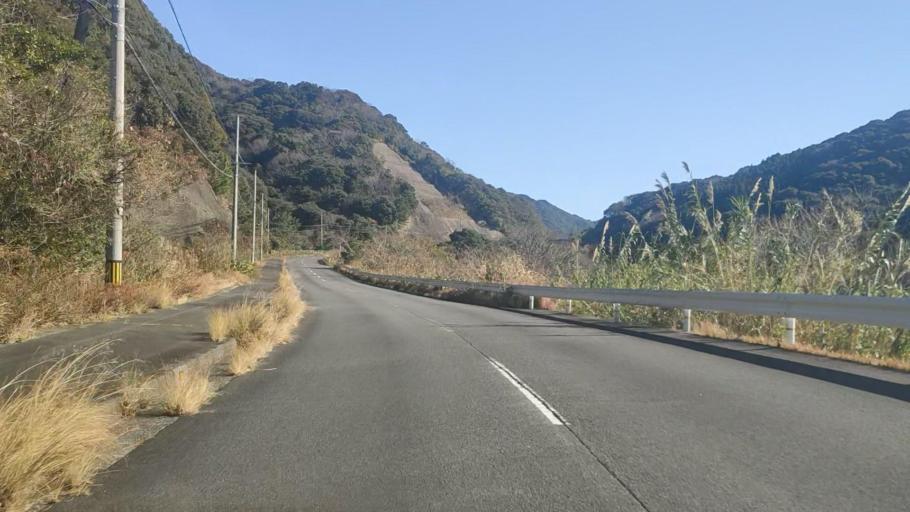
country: JP
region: Oita
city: Saiki
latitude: 32.7949
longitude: 131.8978
